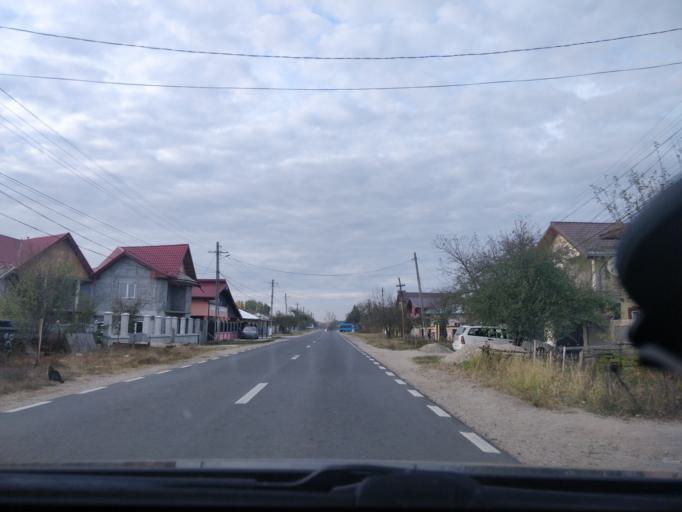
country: RO
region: Giurgiu
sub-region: Comuna Crevedia Mare
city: Dealu
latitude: 44.4075
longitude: 25.6455
